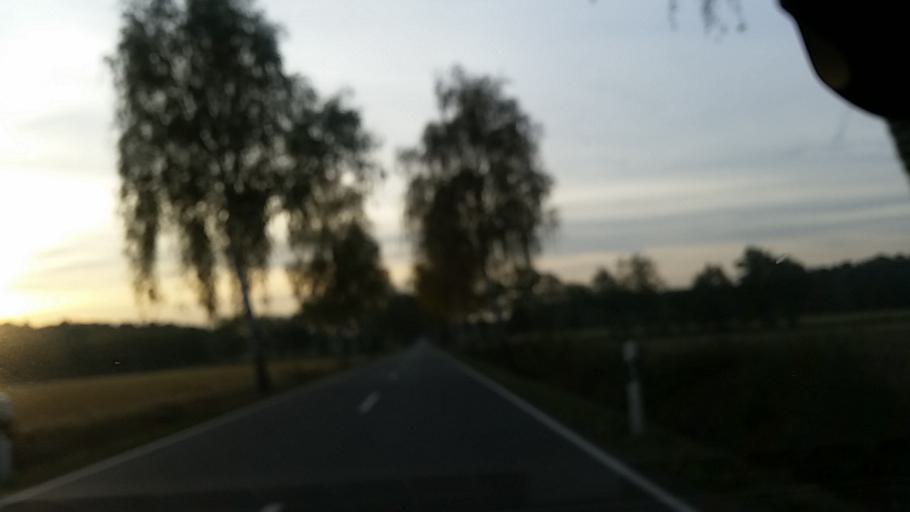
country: DE
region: Lower Saxony
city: Tiddische
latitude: 52.4895
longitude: 10.8077
